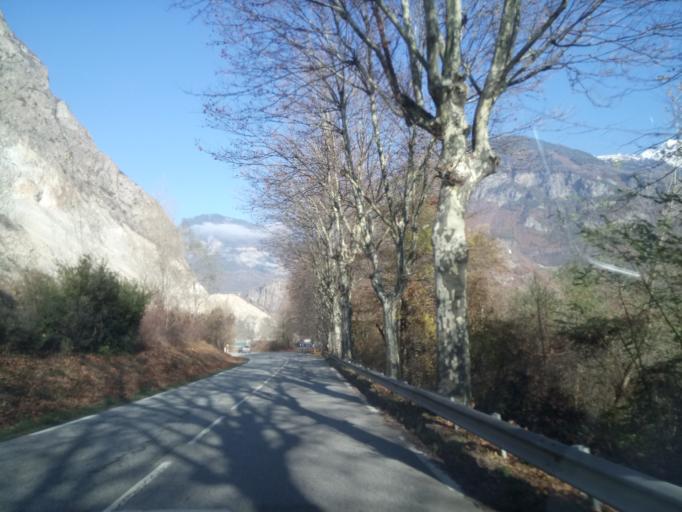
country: FR
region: Rhone-Alpes
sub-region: Departement de la Savoie
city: Saint-Jean-de-Maurienne
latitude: 45.2908
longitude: 6.3530
